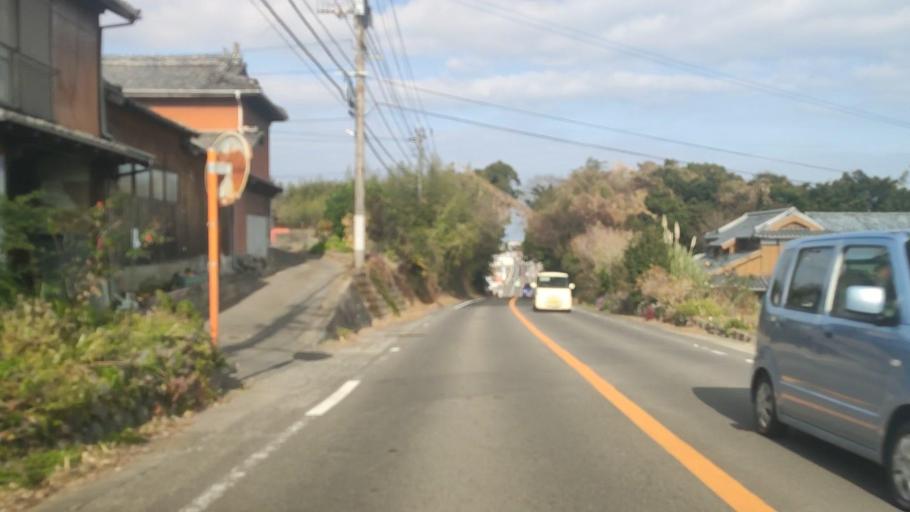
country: JP
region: Nagasaki
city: Shimabara
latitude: 32.6844
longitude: 130.3502
